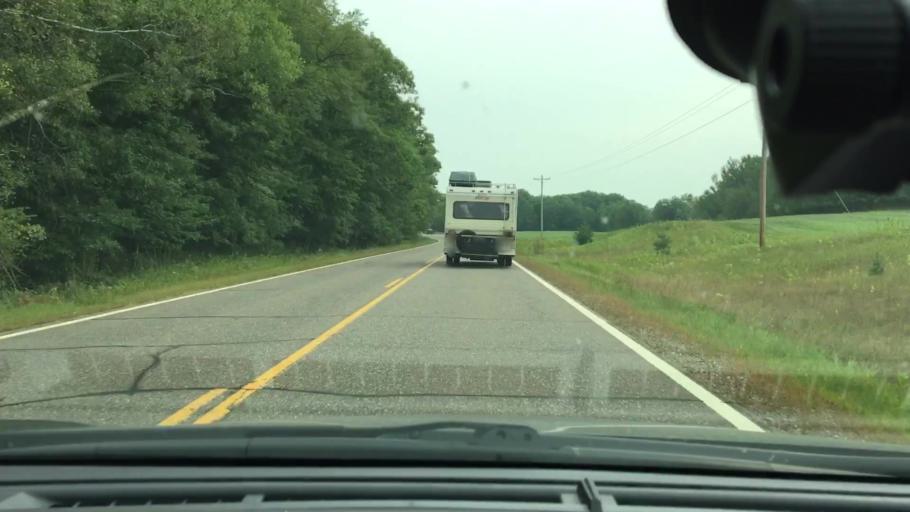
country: US
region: Minnesota
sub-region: Aitkin County
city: Aitkin
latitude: 46.4047
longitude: -93.7861
